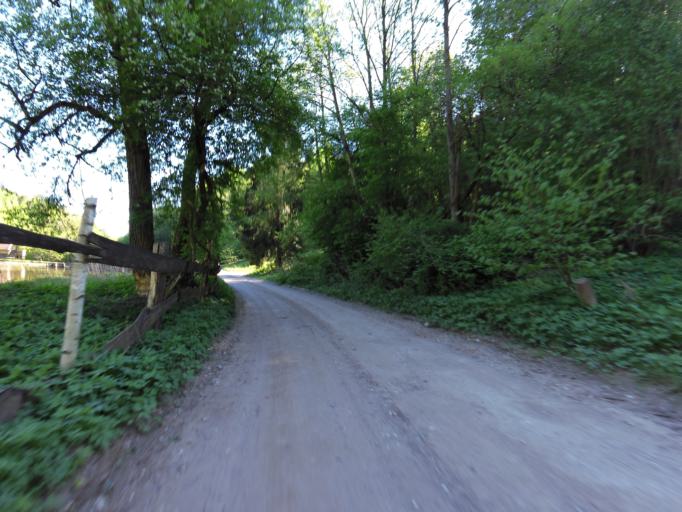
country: LT
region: Vilnius County
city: Pilaite
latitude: 54.6852
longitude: 25.1561
